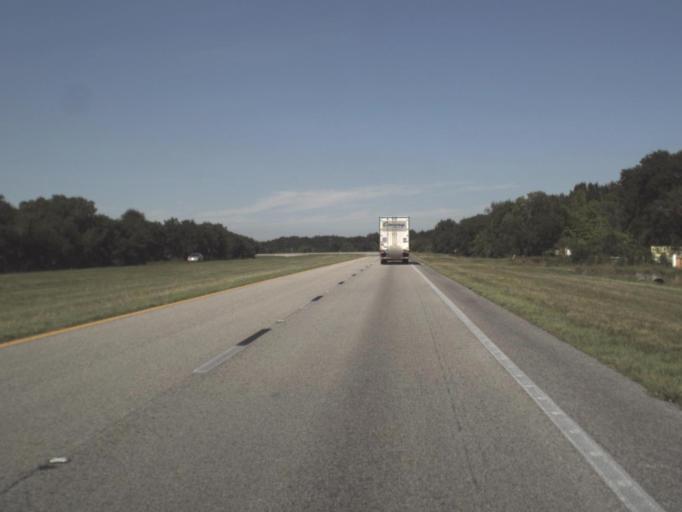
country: US
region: Florida
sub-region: Hendry County
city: Port LaBelle
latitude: 26.9659
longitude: -81.3164
